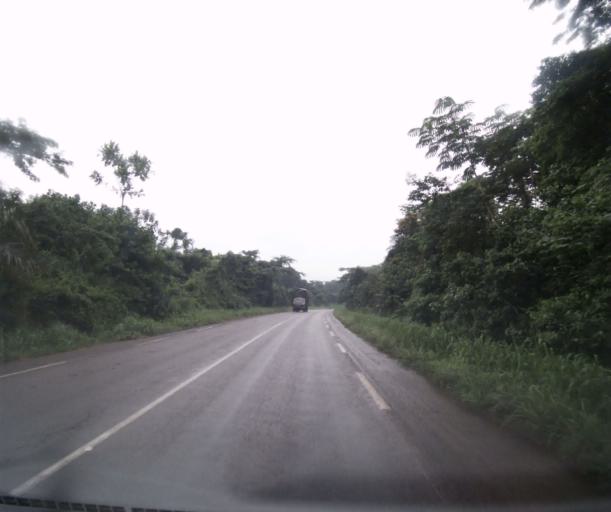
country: CM
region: Centre
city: Eseka
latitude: 3.8639
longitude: 10.5995
